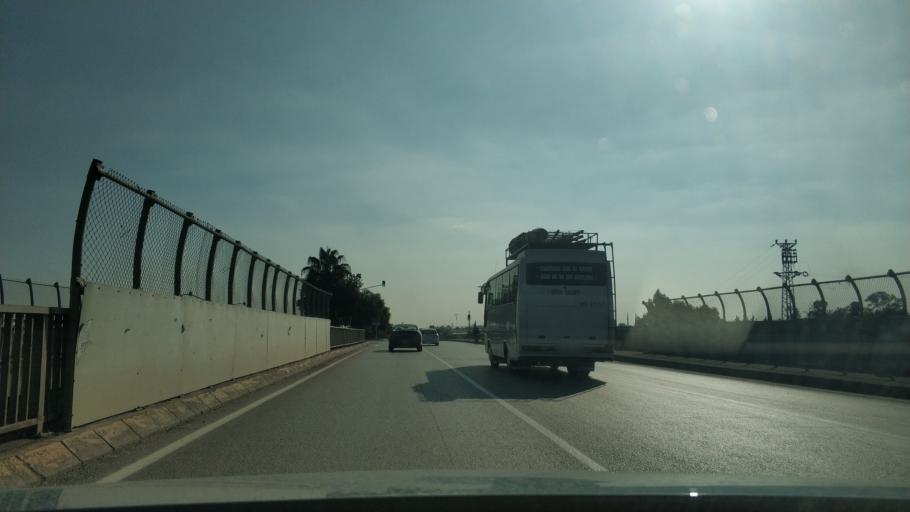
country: TR
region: Adana
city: Seyhan
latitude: 36.9987
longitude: 35.2523
